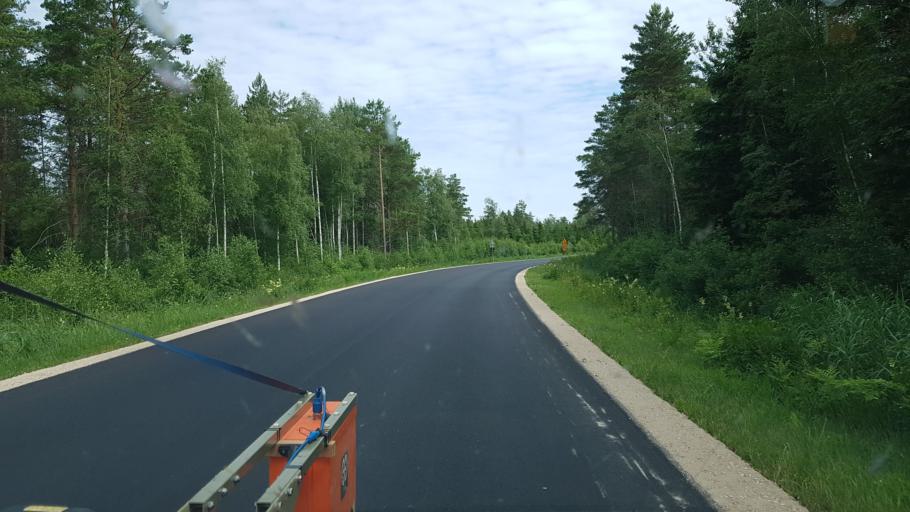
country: EE
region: Paernumaa
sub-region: Audru vald
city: Audru
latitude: 58.6191
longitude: 24.2309
